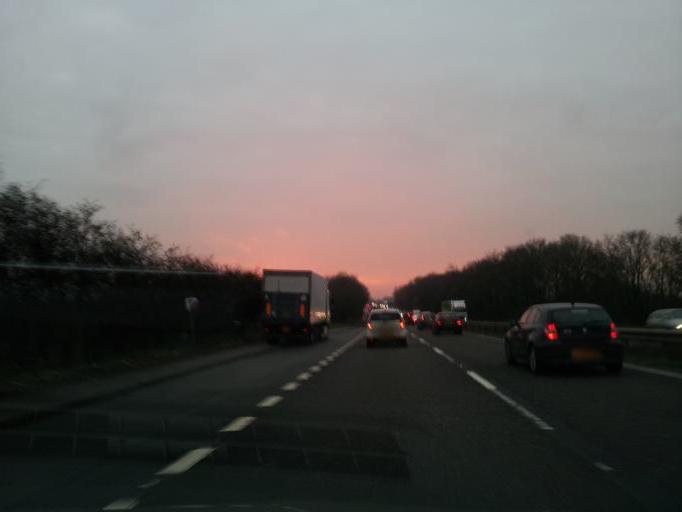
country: GB
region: England
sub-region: Peterborough
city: Wittering
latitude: 52.6066
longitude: -0.4308
